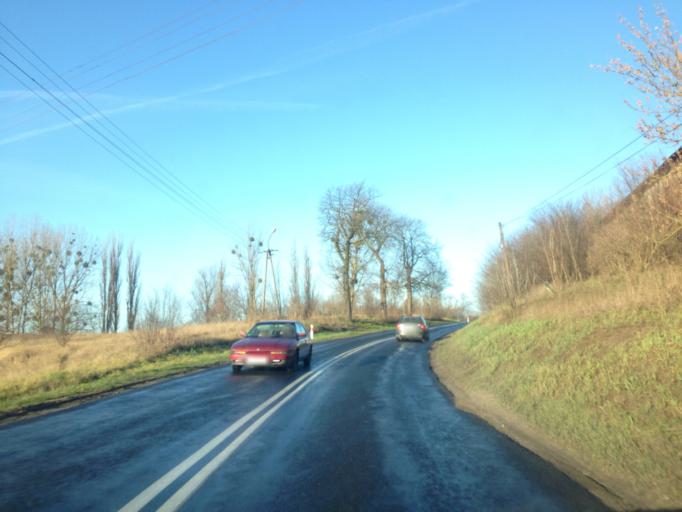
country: PL
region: Kujawsko-Pomorskie
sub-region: Powiat brodnicki
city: Jablonowo Pomorskie
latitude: 53.3424
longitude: 19.2153
